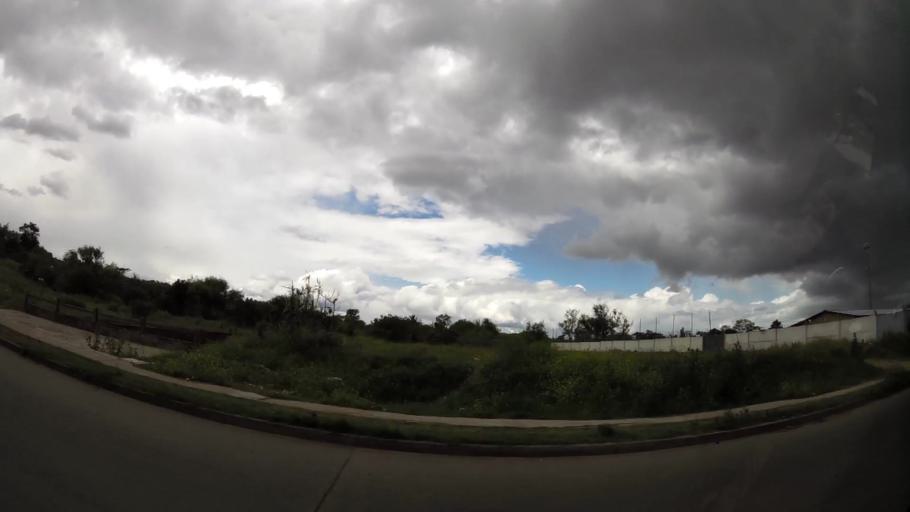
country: UY
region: Montevideo
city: Montevideo
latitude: -34.8373
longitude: -56.1683
